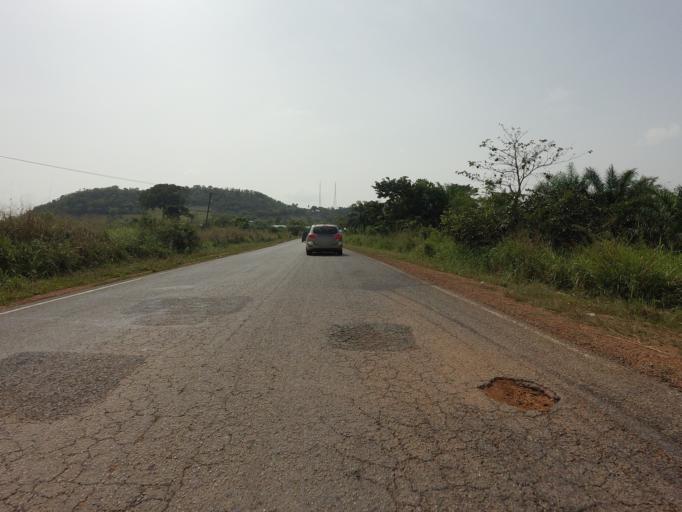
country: GH
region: Volta
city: Ho
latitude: 6.3475
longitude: 0.1746
